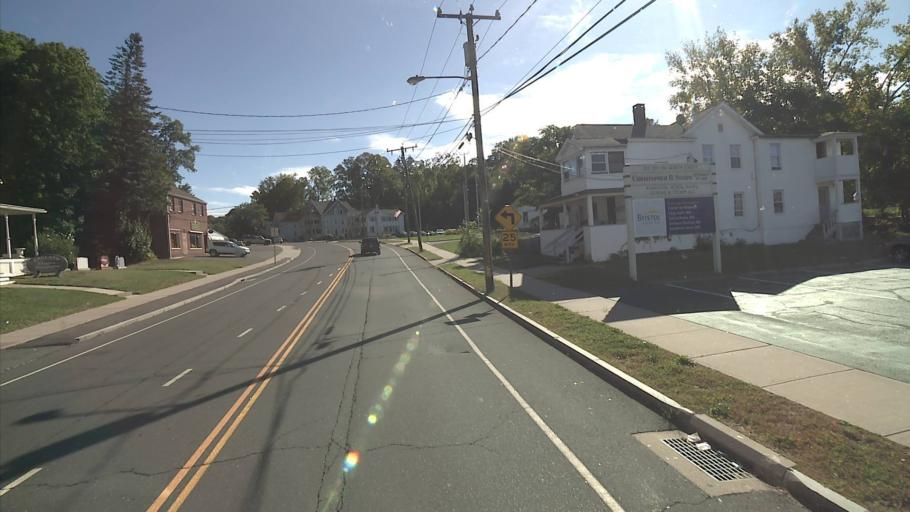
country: US
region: Connecticut
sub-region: Hartford County
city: Bristol
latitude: 41.6812
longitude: -72.9451
